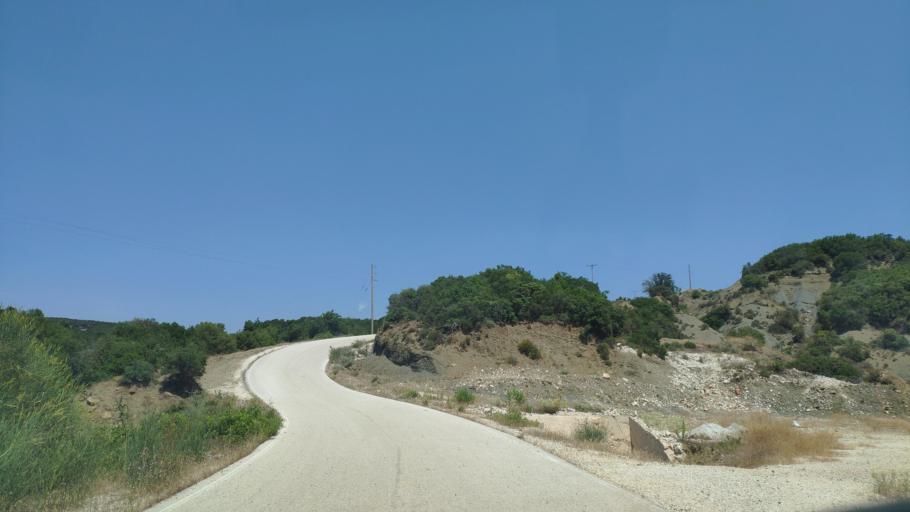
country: GR
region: West Greece
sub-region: Nomos Aitolias kai Akarnanias
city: Sardinia
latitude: 38.8754
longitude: 21.2803
